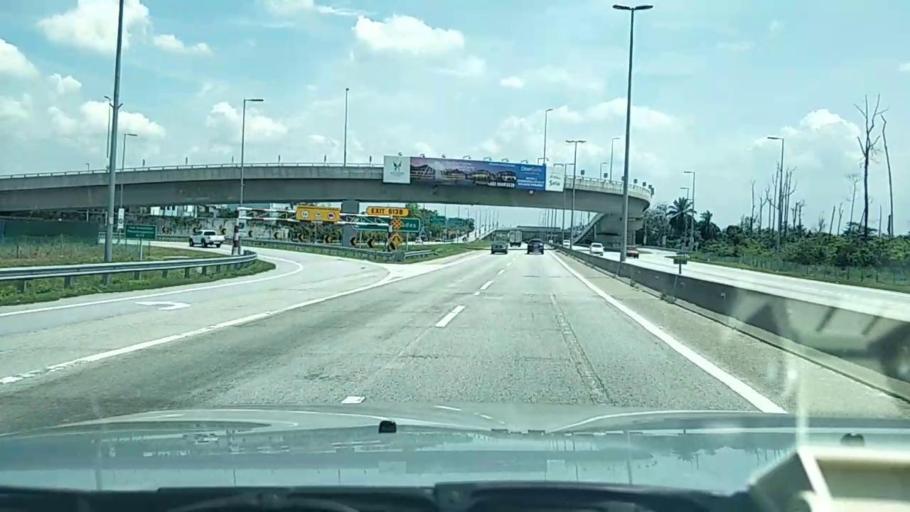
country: MY
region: Putrajaya
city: Putrajaya
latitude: 2.9437
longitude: 101.6321
